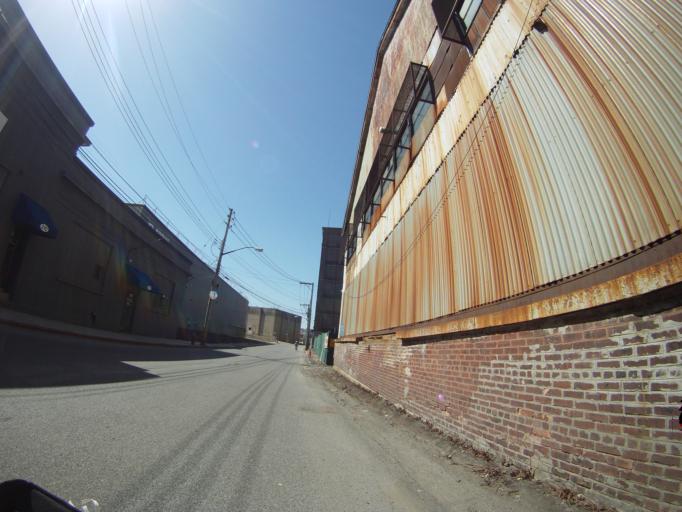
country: US
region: New Jersey
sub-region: Hudson County
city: Bayonne
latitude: 40.6170
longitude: -74.0654
